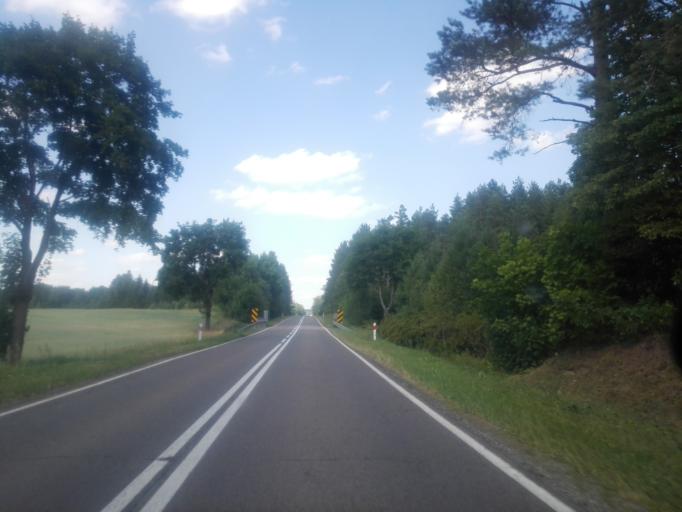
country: PL
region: Podlasie
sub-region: Powiat sejnenski
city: Sejny
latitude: 54.0301
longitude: 23.3500
